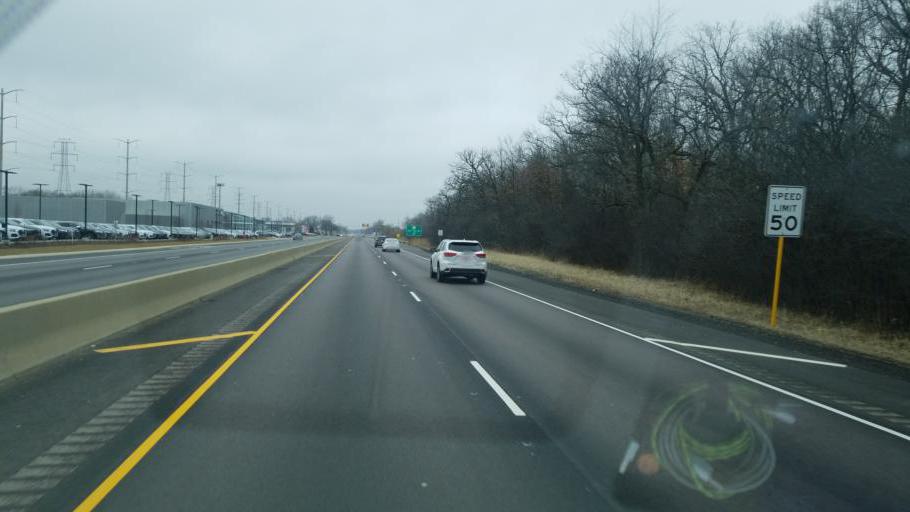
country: US
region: Illinois
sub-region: Lake County
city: Highwood
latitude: 42.1949
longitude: -87.8293
